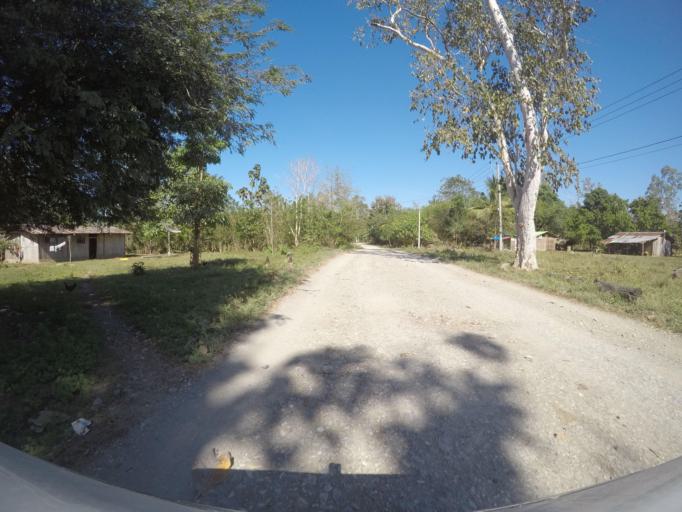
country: TL
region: Viqueque
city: Viqueque
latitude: -8.9333
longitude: 126.1356
